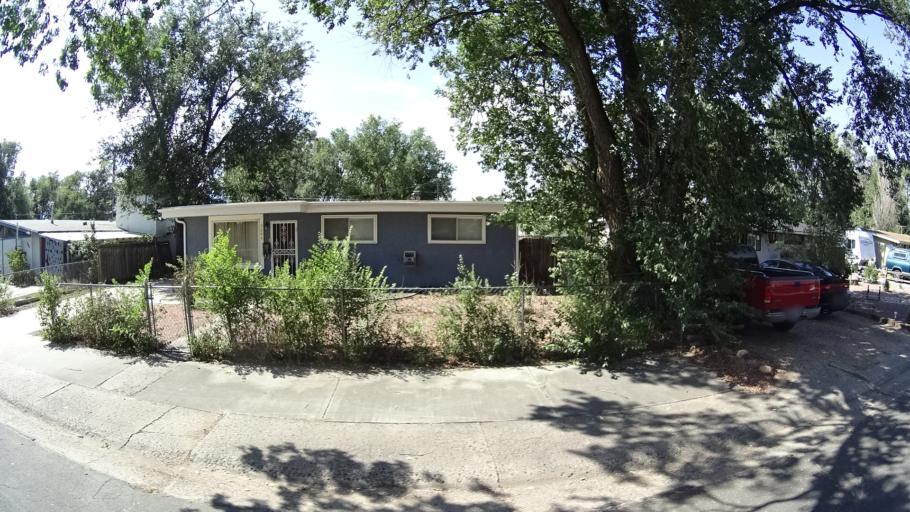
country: US
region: Colorado
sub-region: El Paso County
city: Colorado Springs
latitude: 38.8792
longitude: -104.8105
